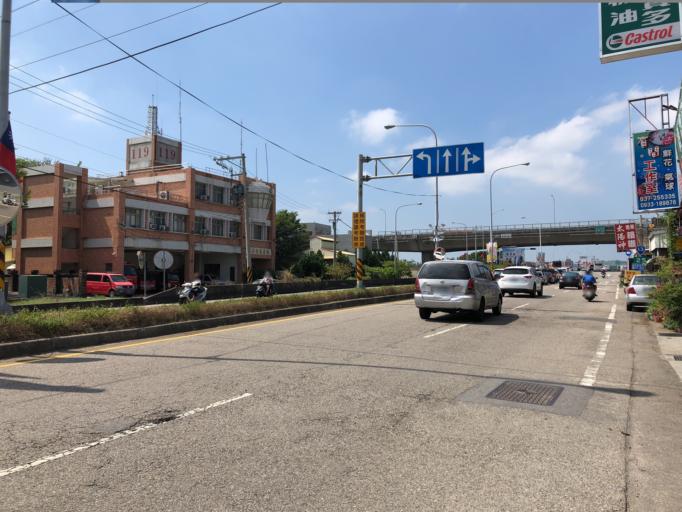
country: TW
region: Taiwan
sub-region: Miaoli
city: Miaoli
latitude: 24.5745
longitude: 120.8479
